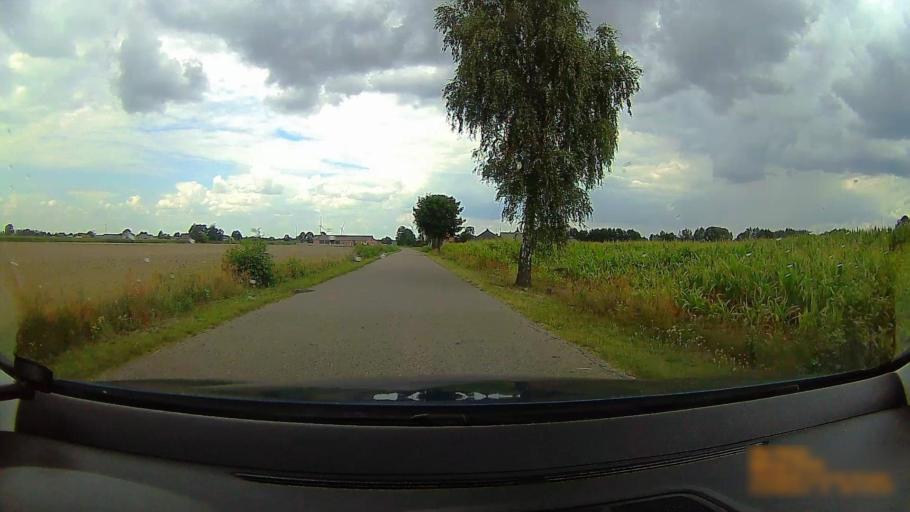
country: PL
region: Greater Poland Voivodeship
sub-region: Powiat koninski
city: Rychwal
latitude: 52.1047
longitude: 18.1911
